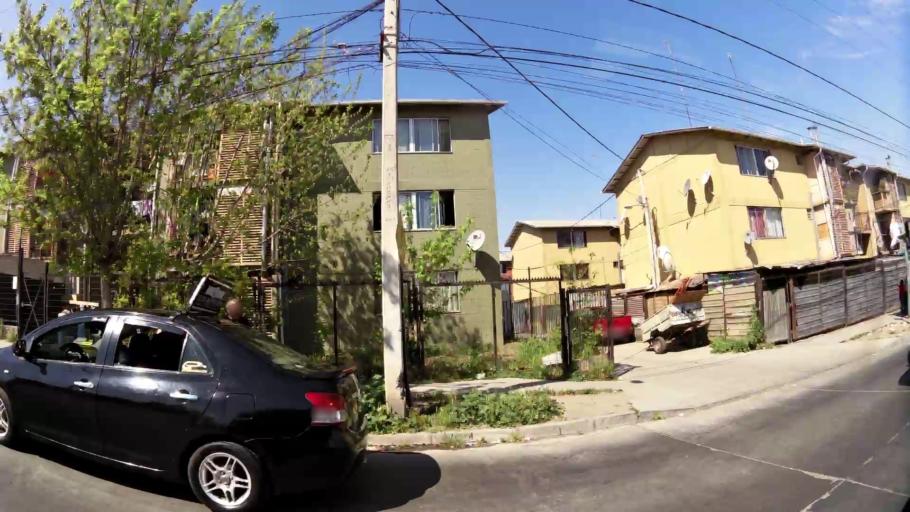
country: CL
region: Santiago Metropolitan
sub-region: Provincia de Cordillera
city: Puente Alto
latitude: -33.6280
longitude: -70.6073
